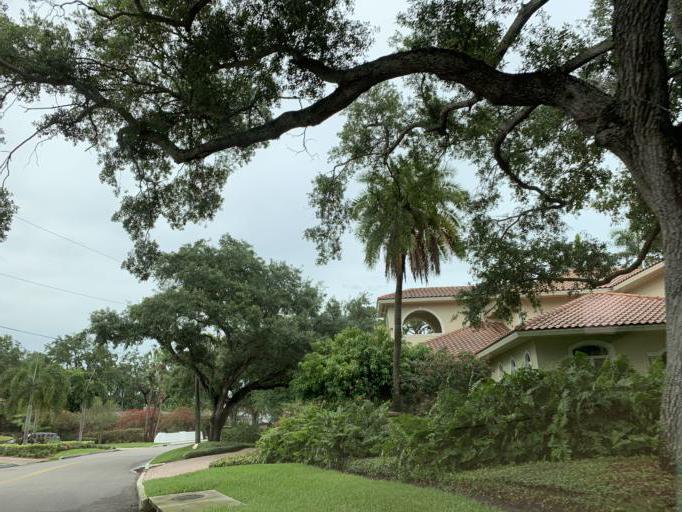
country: US
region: Florida
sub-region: Pinellas County
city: Saint Petersburg
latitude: 27.7937
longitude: -82.6210
